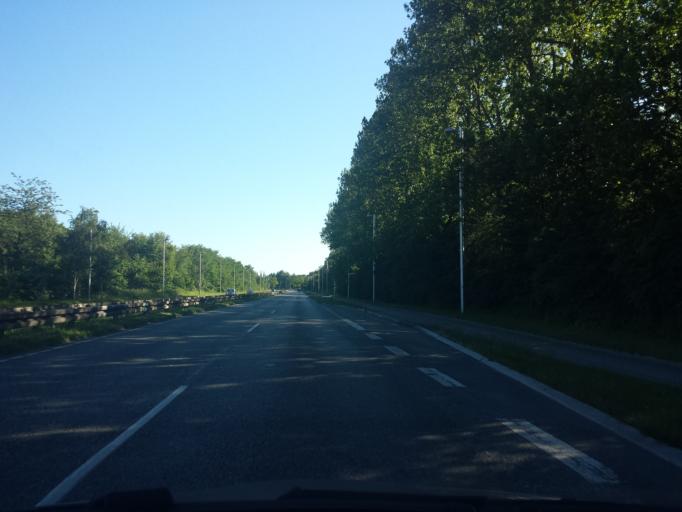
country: DK
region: Capital Region
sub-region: Glostrup Kommune
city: Glostrup
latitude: 55.6892
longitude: 12.4039
